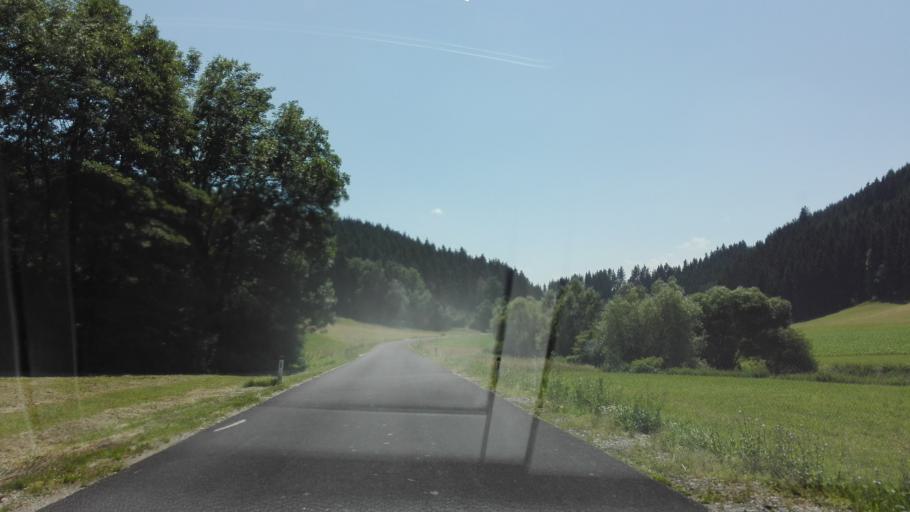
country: AT
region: Upper Austria
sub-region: Politischer Bezirk Grieskirchen
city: Bad Schallerbach
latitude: 48.3585
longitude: 13.8906
